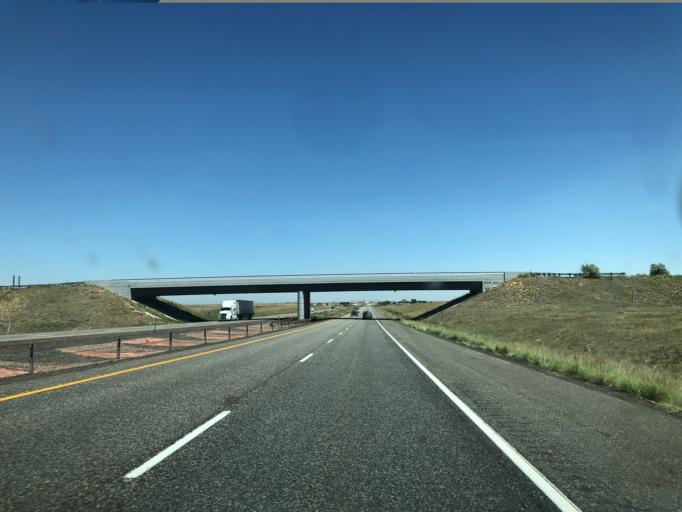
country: US
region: Colorado
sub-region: Adams County
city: Aurora
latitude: 39.7533
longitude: -104.7165
